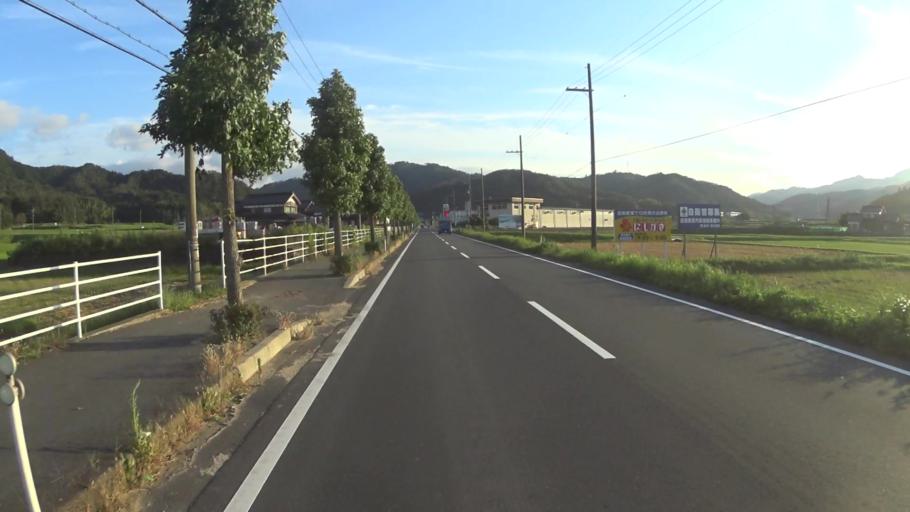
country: JP
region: Kyoto
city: Miyazu
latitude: 35.5731
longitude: 135.0978
